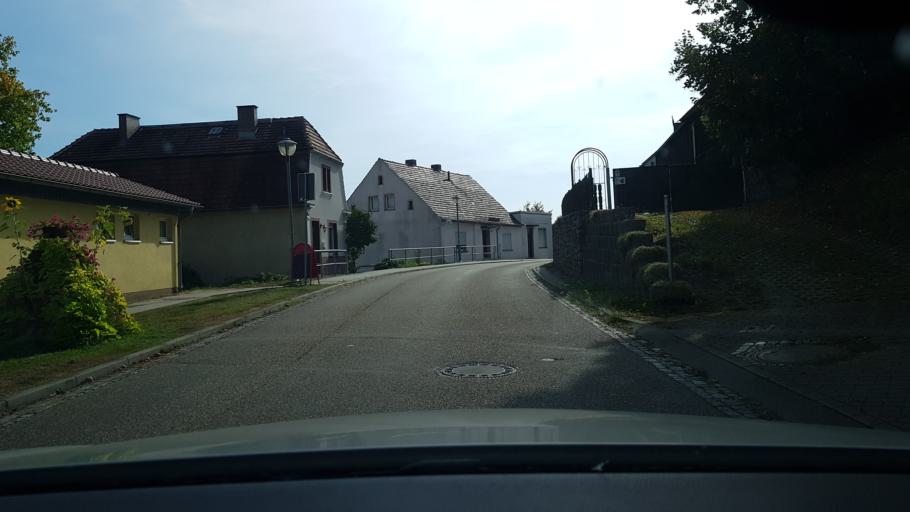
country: DE
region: Brandenburg
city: Neuzelle
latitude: 52.0944
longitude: 14.6487
